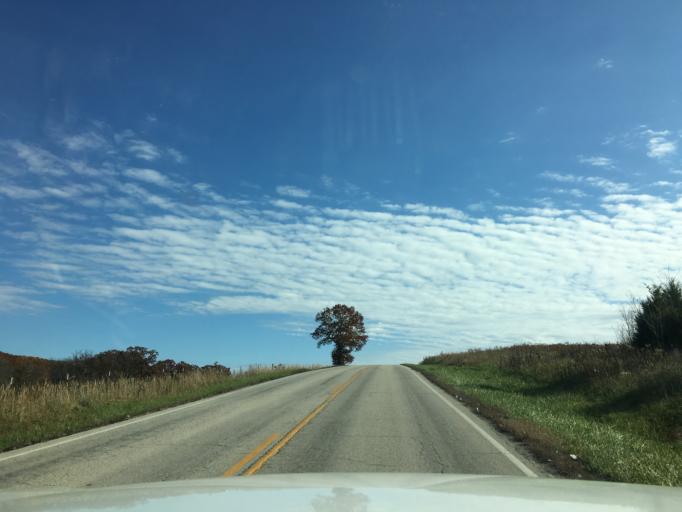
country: US
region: Missouri
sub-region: Maries County
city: Belle
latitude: 38.3369
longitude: -91.7811
